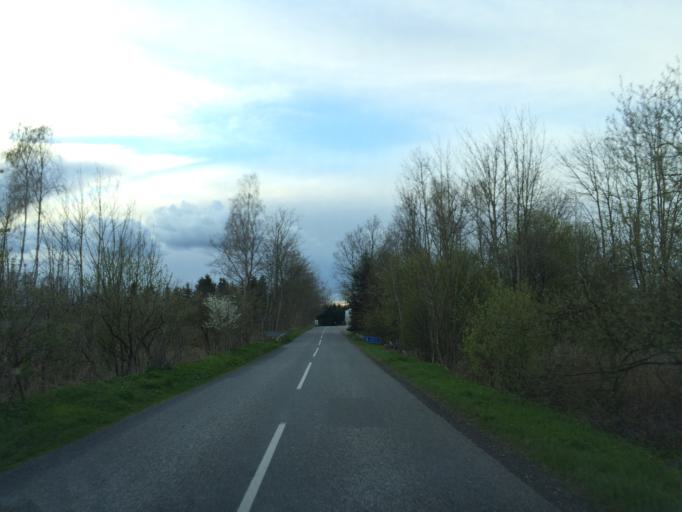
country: DK
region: South Denmark
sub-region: Odense Kommune
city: Bellinge
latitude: 55.2901
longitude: 10.2884
